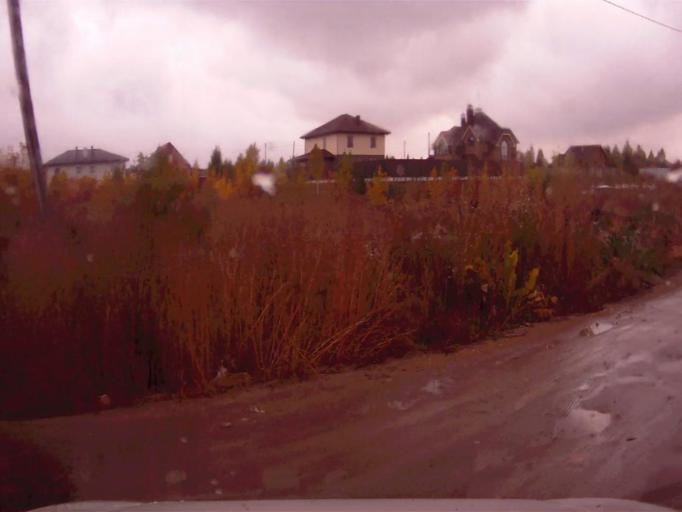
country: RU
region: Chelyabinsk
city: Dolgoderevenskoye
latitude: 55.3095
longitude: 61.3412
